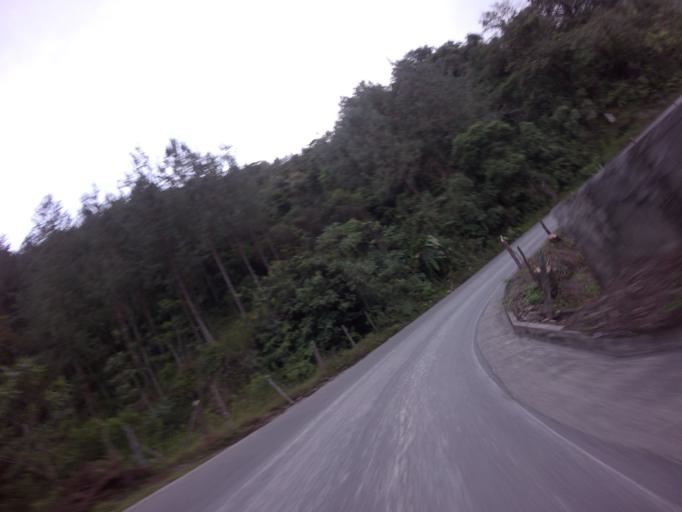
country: CO
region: Caldas
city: Manzanares
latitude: 5.2896
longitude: -75.1484
